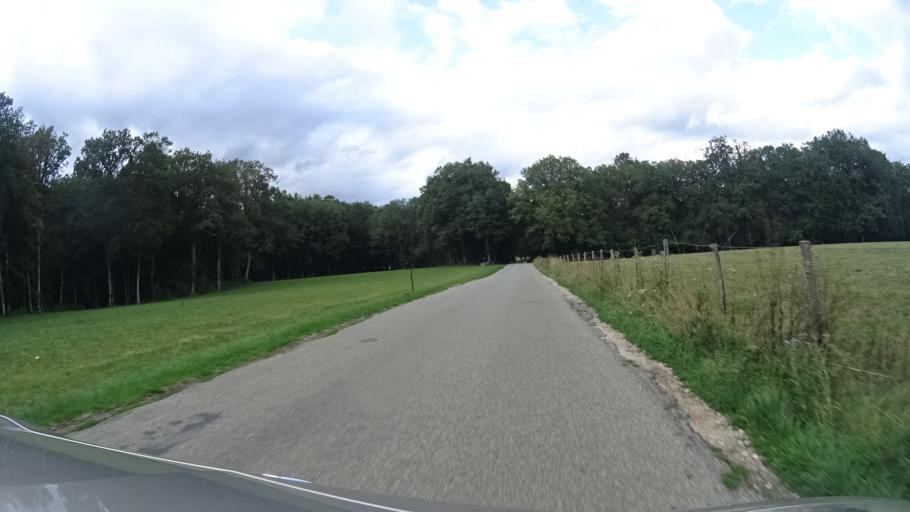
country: FR
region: Franche-Comte
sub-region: Departement du Doubs
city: Nancray
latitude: 47.2299
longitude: 6.1625
